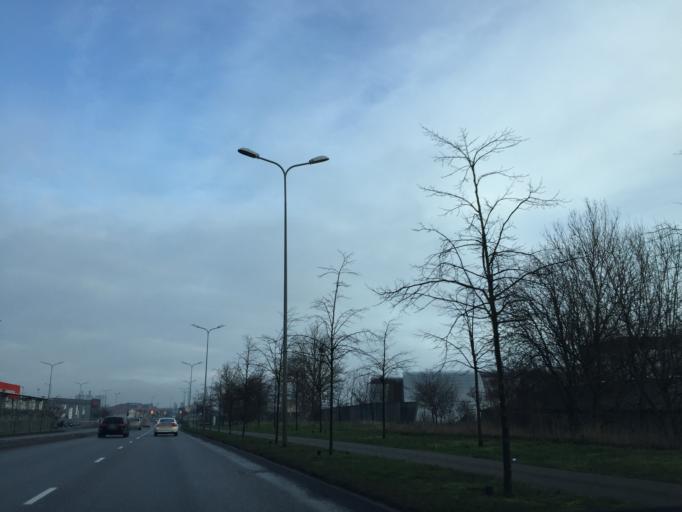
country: LV
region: Liepaja
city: Liepaja
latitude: 56.5147
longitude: 21.0229
